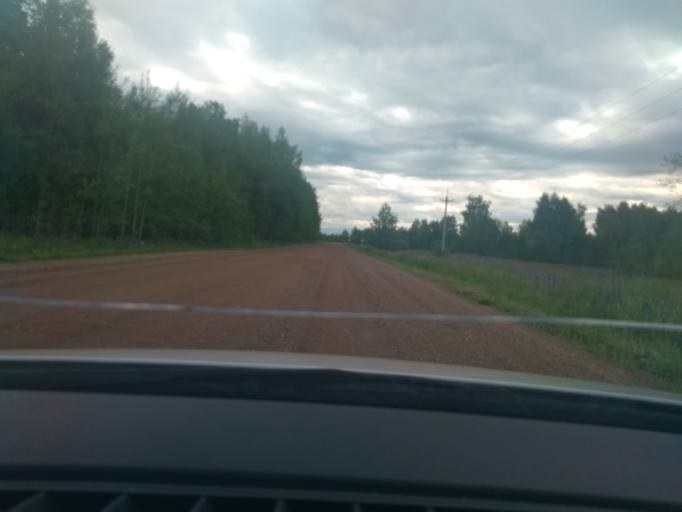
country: RU
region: Perm
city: Sylva
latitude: 57.8177
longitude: 56.7238
